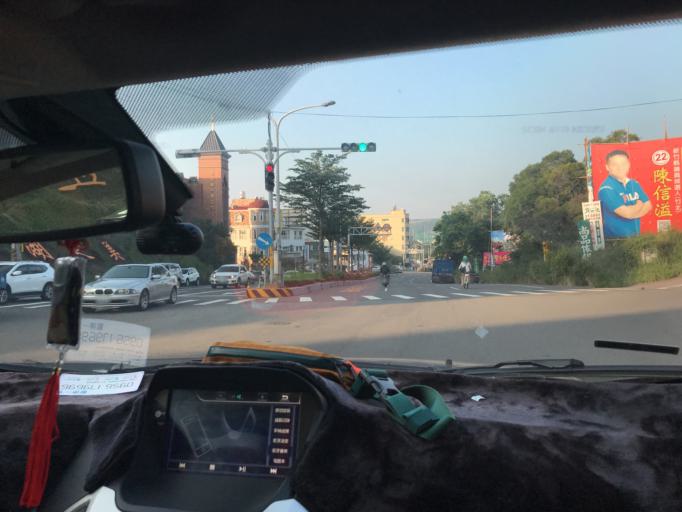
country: TW
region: Taiwan
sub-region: Hsinchu
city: Zhubei
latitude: 24.8284
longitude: 121.0357
